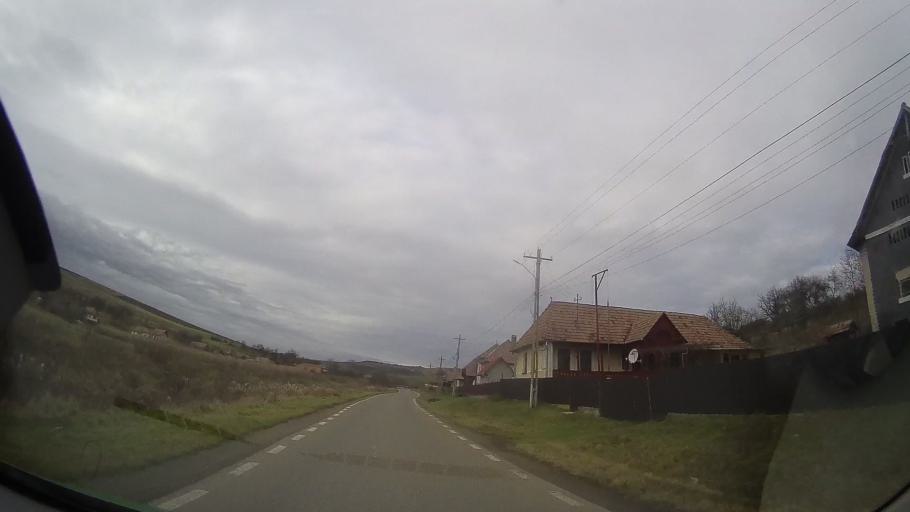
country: RO
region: Mures
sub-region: Comuna Cozma
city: Cozma
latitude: 46.8111
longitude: 24.5074
